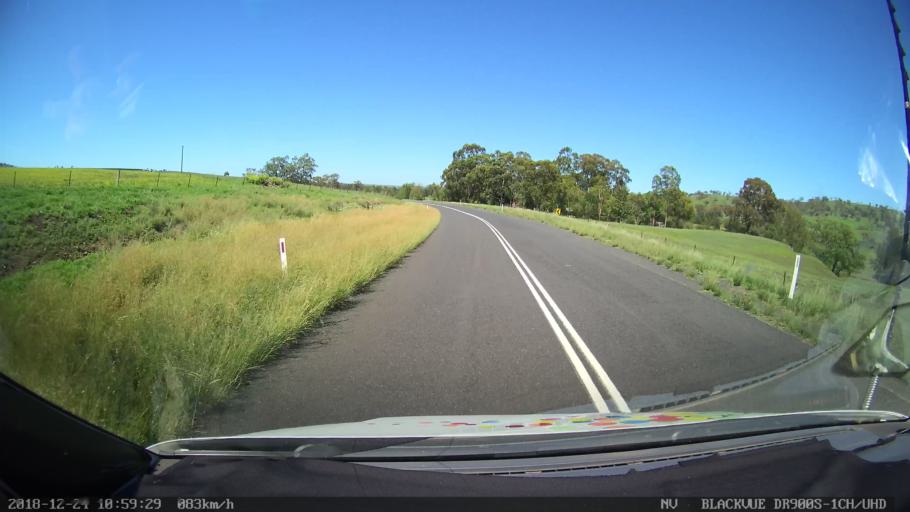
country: AU
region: New South Wales
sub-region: Upper Hunter Shire
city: Merriwa
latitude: -32.0651
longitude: 150.3938
